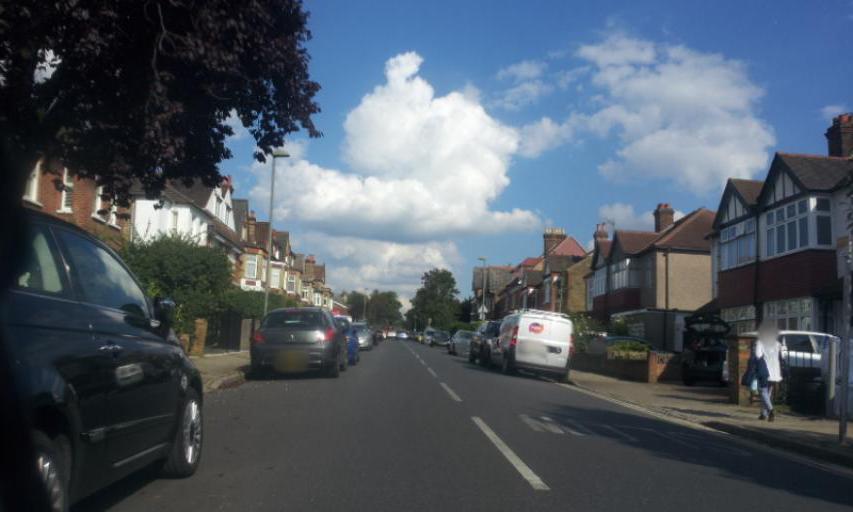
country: GB
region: England
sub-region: Greater London
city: Bromley
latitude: 51.3985
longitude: 0.0375
